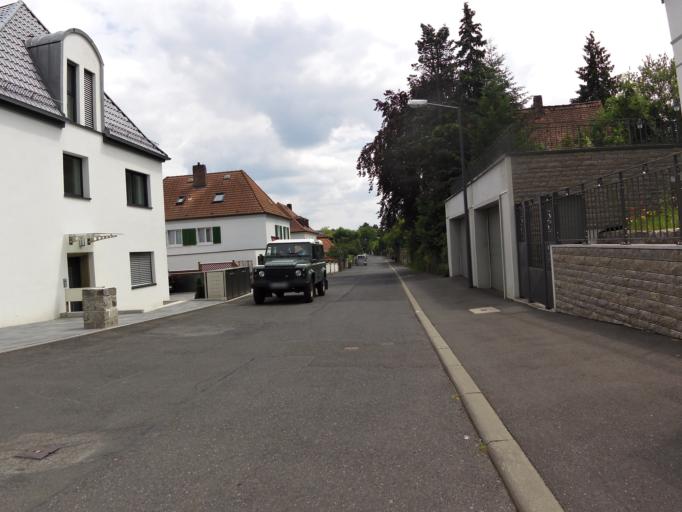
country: DE
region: Bavaria
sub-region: Regierungsbezirk Unterfranken
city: Wuerzburg
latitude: 49.7709
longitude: 9.9286
